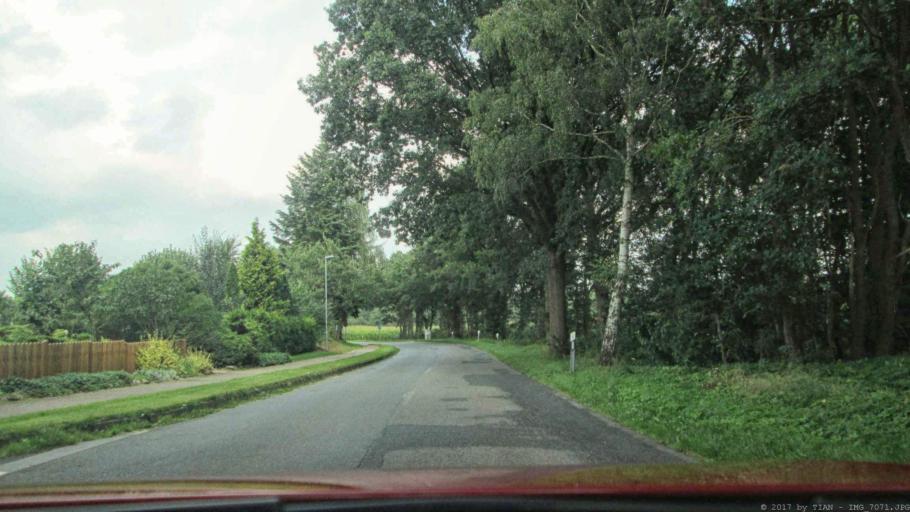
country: DE
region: Lower Saxony
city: Thomasburg
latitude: 53.2256
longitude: 10.6550
